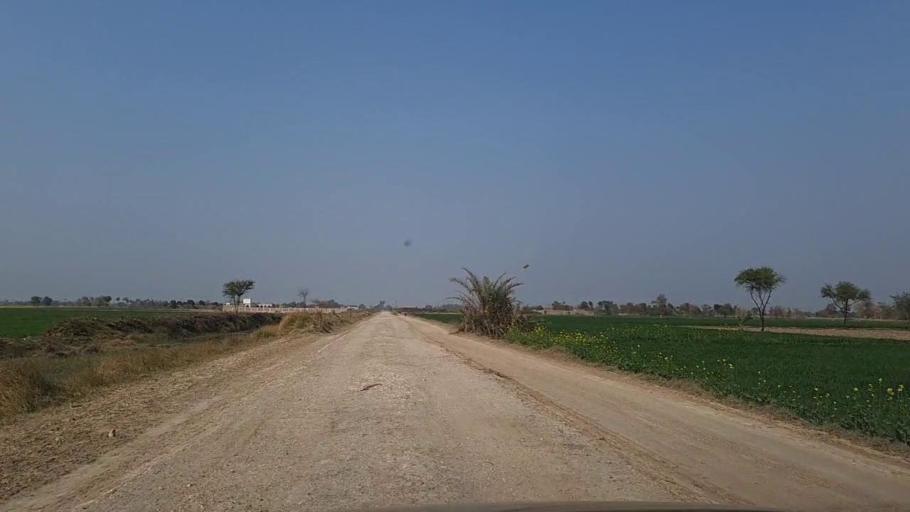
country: PK
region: Sindh
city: Daur
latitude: 26.4167
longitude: 68.4088
